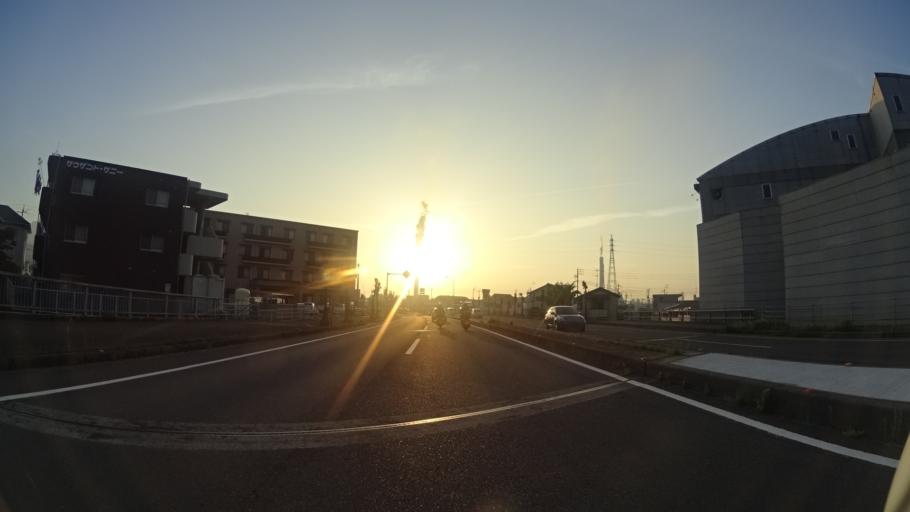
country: JP
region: Ehime
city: Kawanoecho
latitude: 33.9872
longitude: 133.5661
